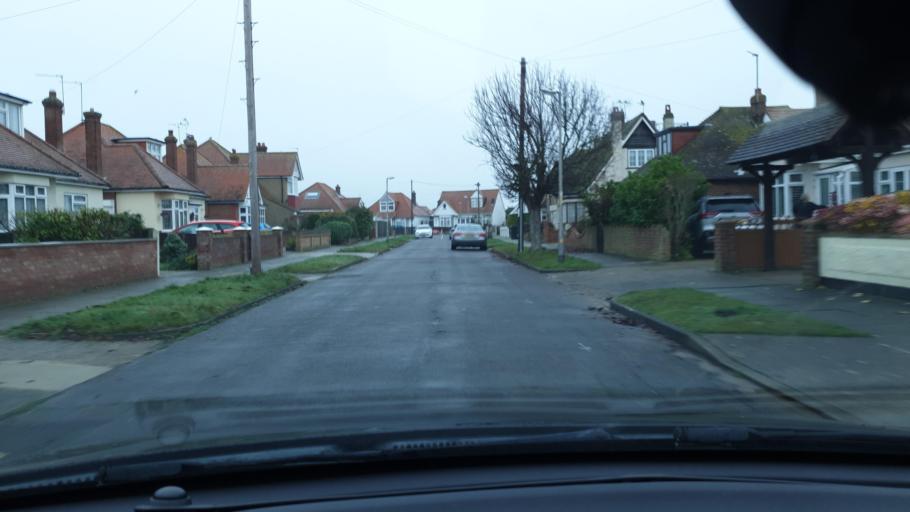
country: GB
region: England
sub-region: Essex
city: Clacton-on-Sea
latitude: 51.8015
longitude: 1.1893
